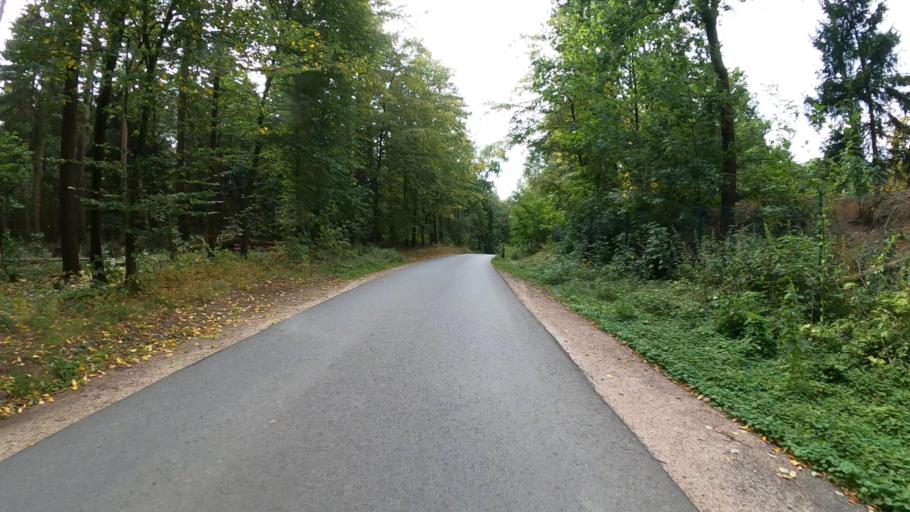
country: DE
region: Lower Saxony
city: Wenzendorf
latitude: 53.3651
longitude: 9.7567
